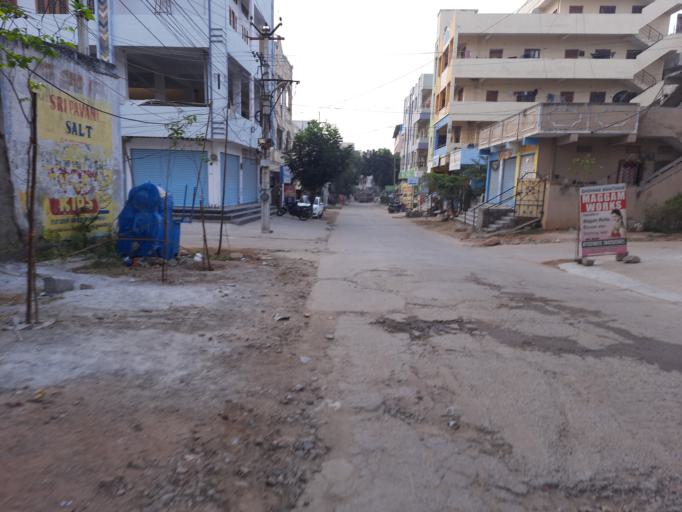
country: IN
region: Telangana
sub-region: Rangareddi
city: Uppal Kalan
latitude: 17.4146
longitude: 78.5710
